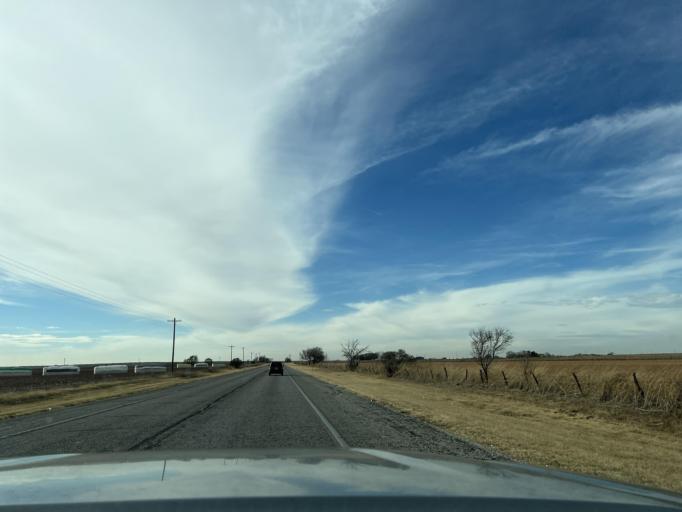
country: US
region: Texas
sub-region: Fisher County
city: Roby
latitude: 32.7579
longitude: -100.2819
